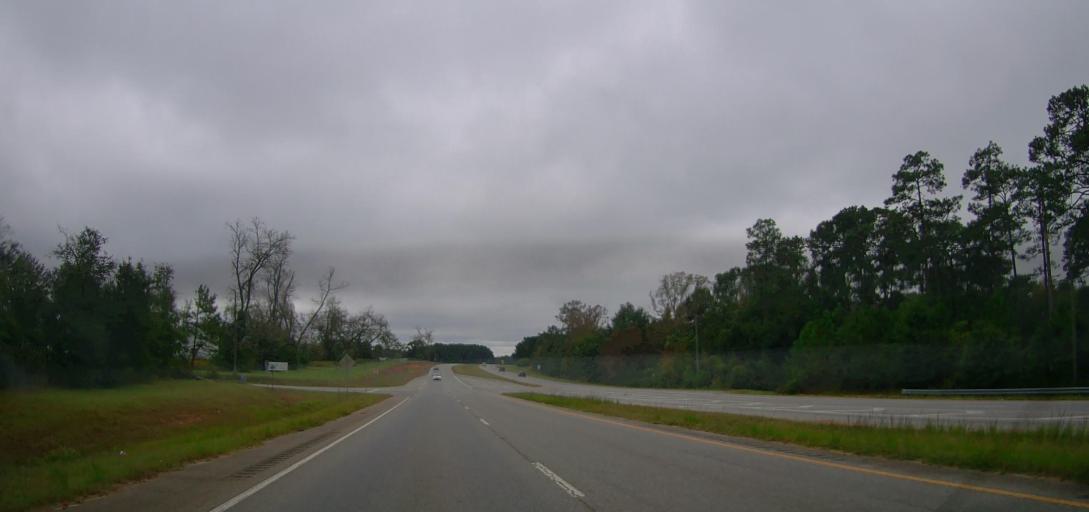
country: US
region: Georgia
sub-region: Thomas County
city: Thomasville
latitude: 30.8668
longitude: -84.0063
